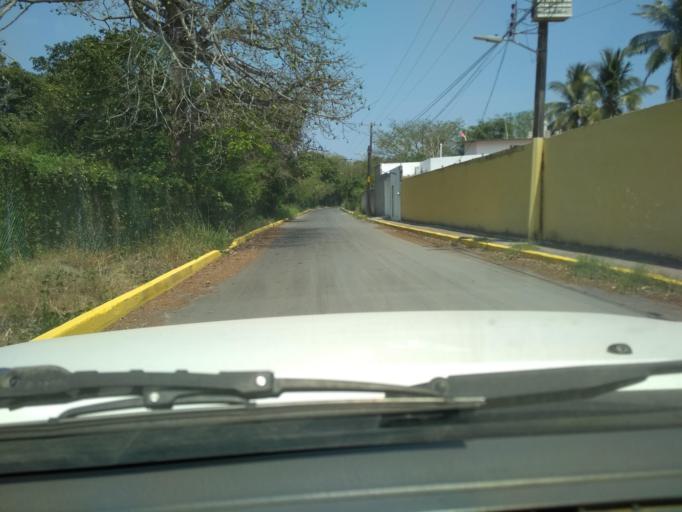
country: MX
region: Veracruz
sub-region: Medellin
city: Fraccionamiento Arboledas San Ramon
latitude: 19.0902
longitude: -96.1428
